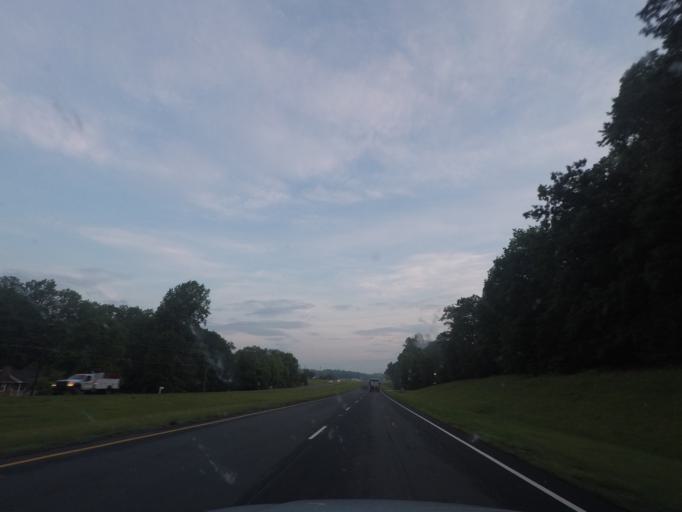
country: US
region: North Carolina
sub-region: Person County
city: Roxboro
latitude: 36.2494
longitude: -78.9394
